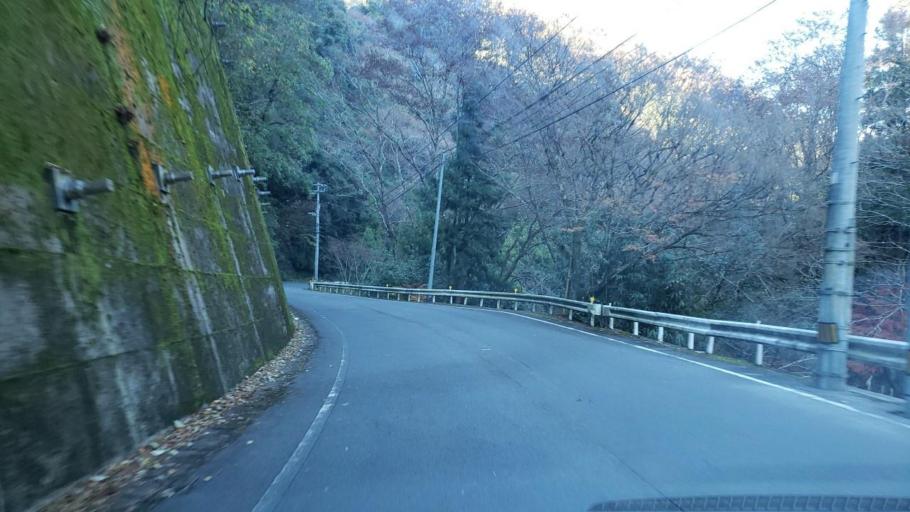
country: JP
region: Tokushima
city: Wakimachi
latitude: 34.0125
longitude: 134.0319
